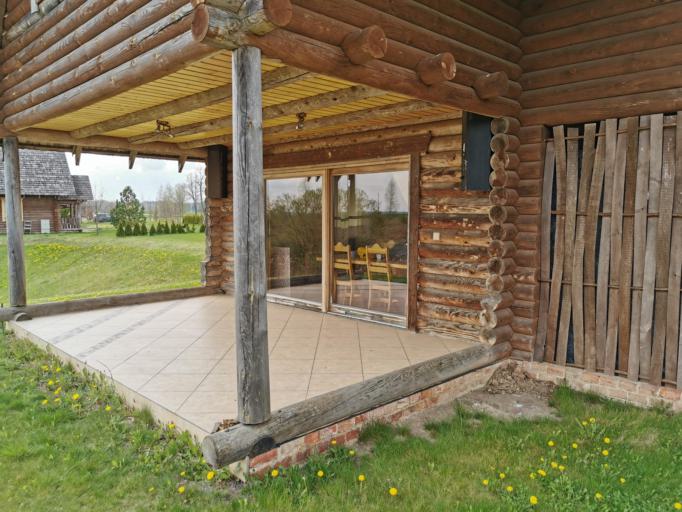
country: LT
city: Vilkija
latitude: 55.1366
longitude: 23.7688
